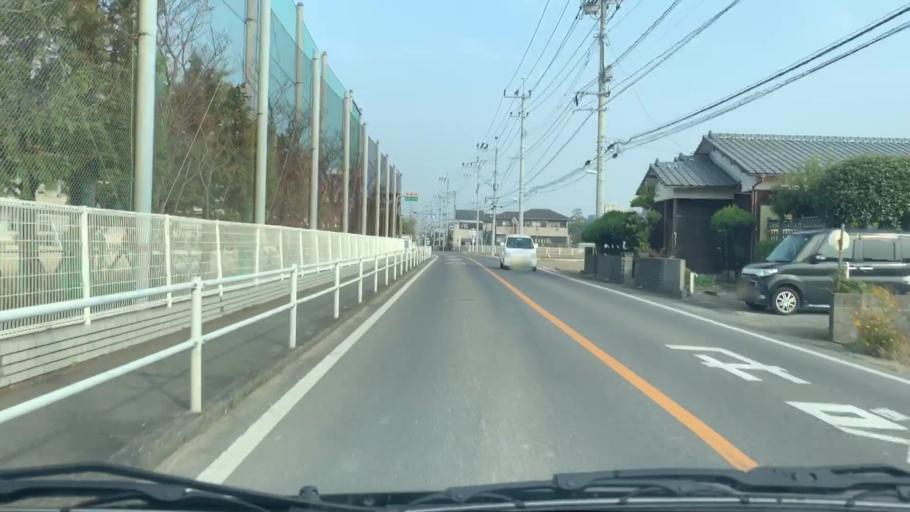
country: JP
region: Saga Prefecture
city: Saga-shi
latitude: 33.2400
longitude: 130.2584
